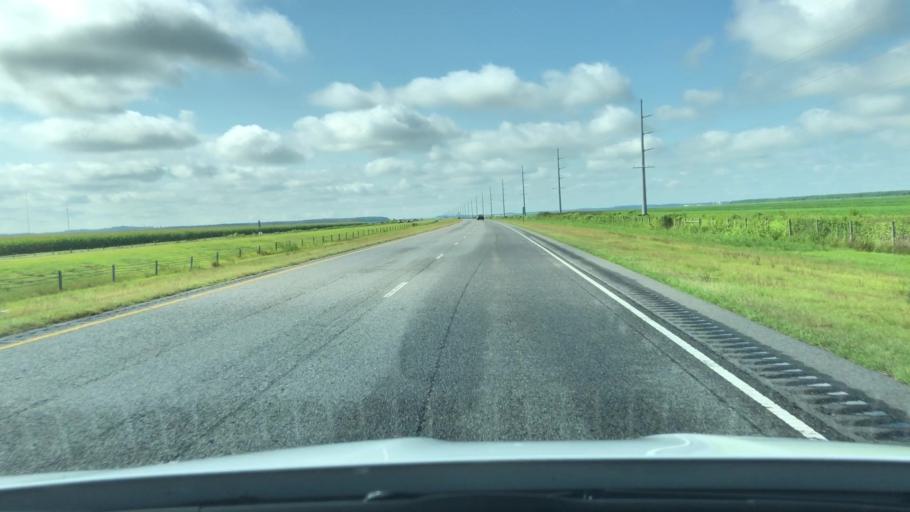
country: US
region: North Carolina
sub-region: Pasquotank County
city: Elizabeth City
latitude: 36.3337
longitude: -76.3121
